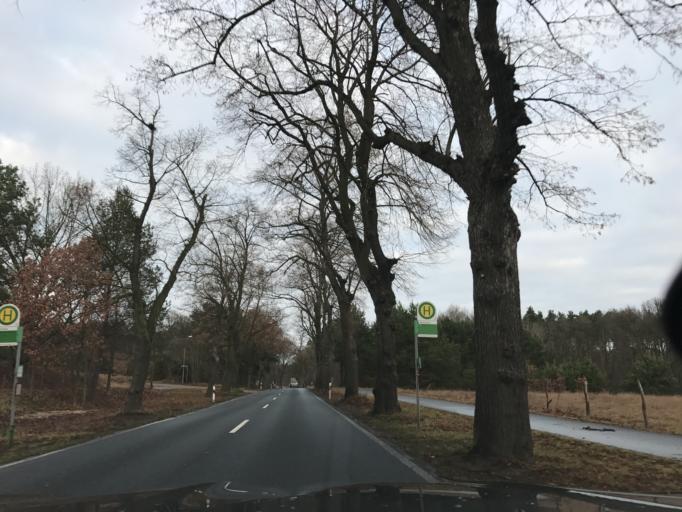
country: DE
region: Brandenburg
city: Gross Kreutz
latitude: 52.3248
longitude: 12.7326
